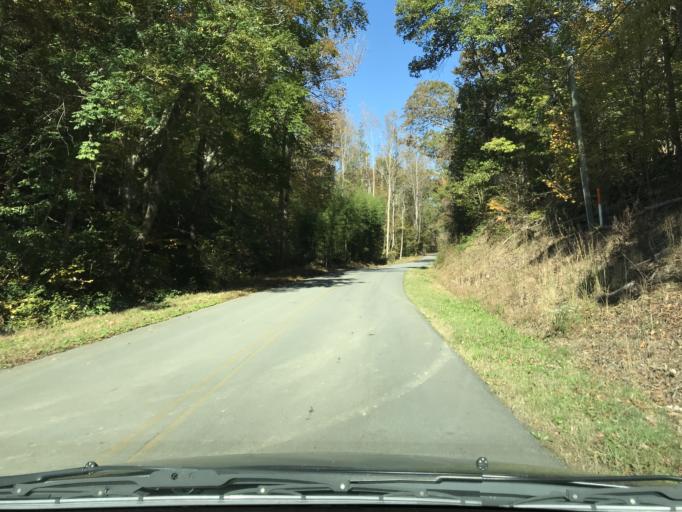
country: US
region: Georgia
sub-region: Dade County
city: Trenton
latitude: 34.9047
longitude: -85.4643
